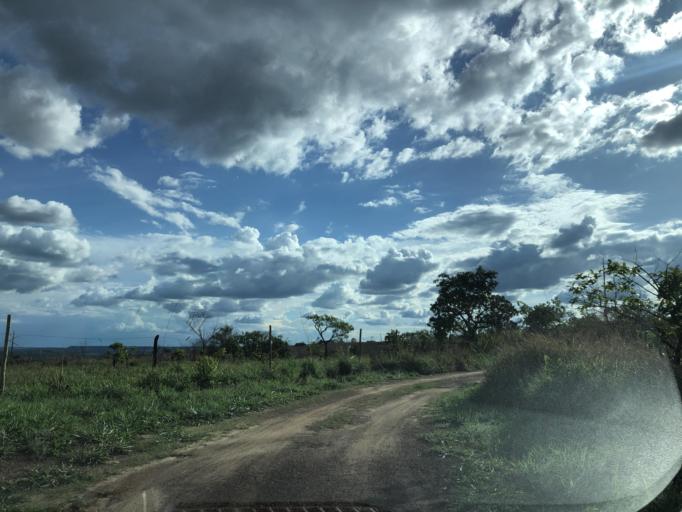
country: BR
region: Goias
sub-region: Luziania
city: Luziania
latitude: -16.0162
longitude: -48.1375
